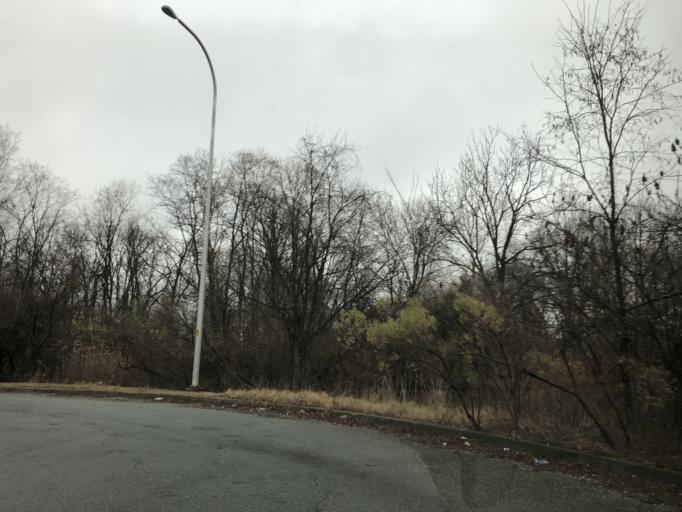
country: US
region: Delaware
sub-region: New Castle County
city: Wilmington
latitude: 39.7153
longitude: -75.5636
